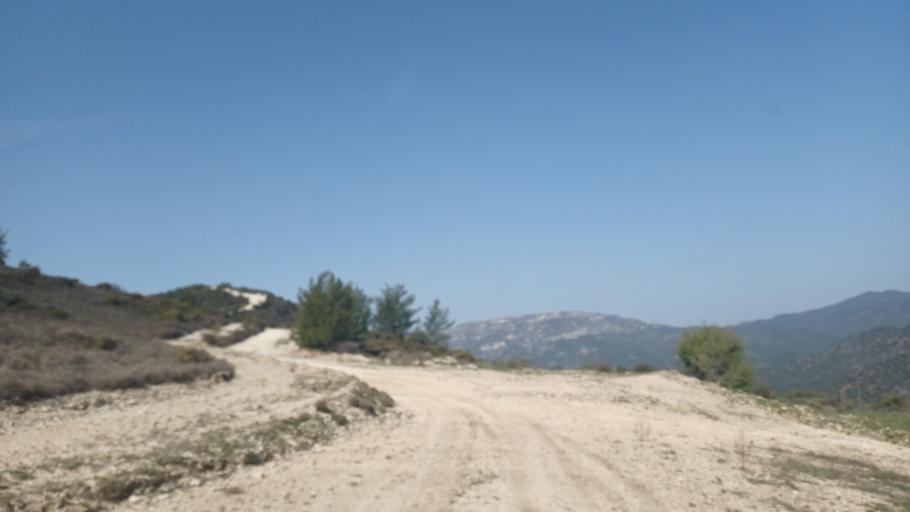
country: CY
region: Limassol
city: Pachna
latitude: 34.8876
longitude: 32.7272
